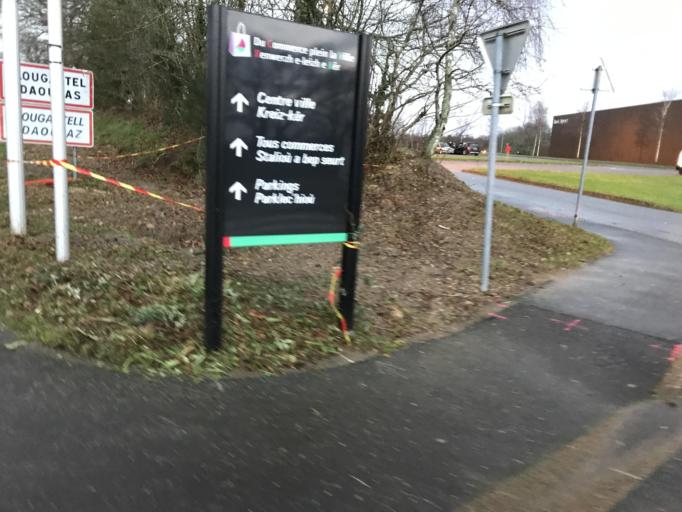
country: FR
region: Brittany
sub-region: Departement du Finistere
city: Plougastel-Daoulas
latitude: 48.3691
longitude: -4.3616
